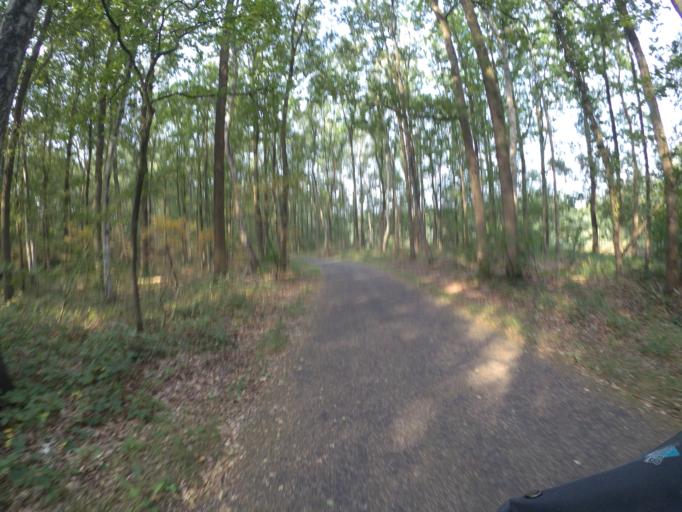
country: NL
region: North Brabant
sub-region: Gemeente Waalwijk
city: Waalwijk
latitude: 51.6759
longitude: 5.0967
